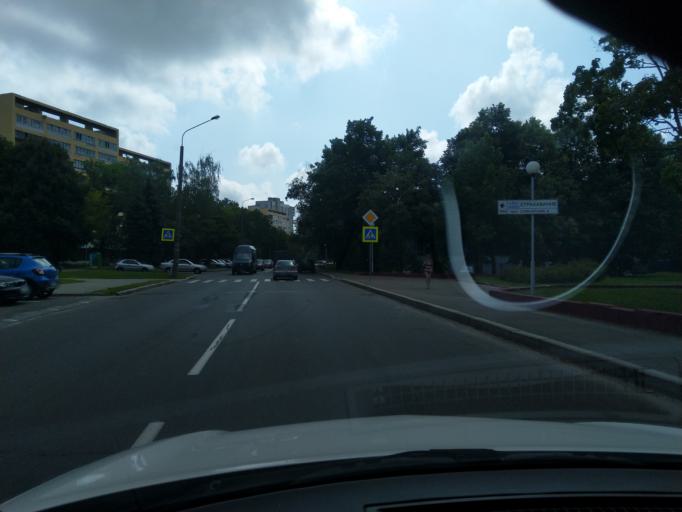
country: BY
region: Minsk
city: Minsk
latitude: 53.8981
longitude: 27.5776
